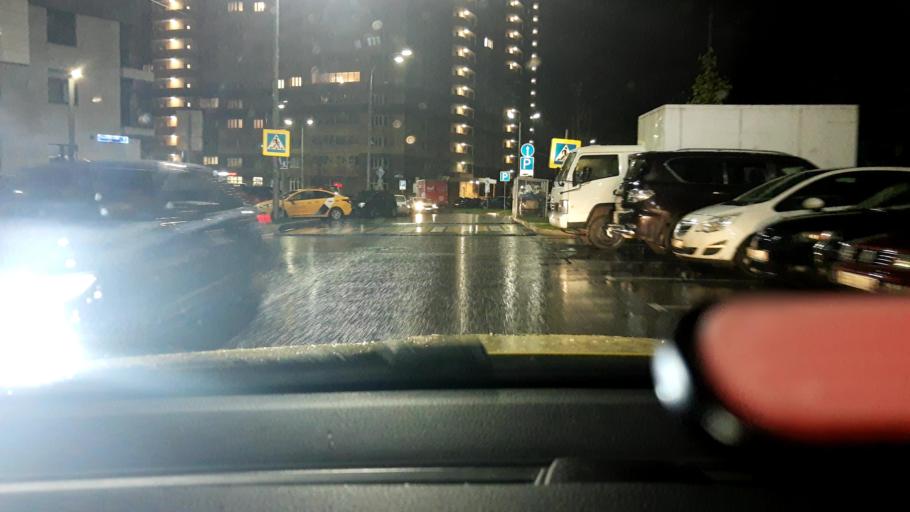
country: RU
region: Moscow
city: Zhulebino
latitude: 55.6697
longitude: 37.8545
